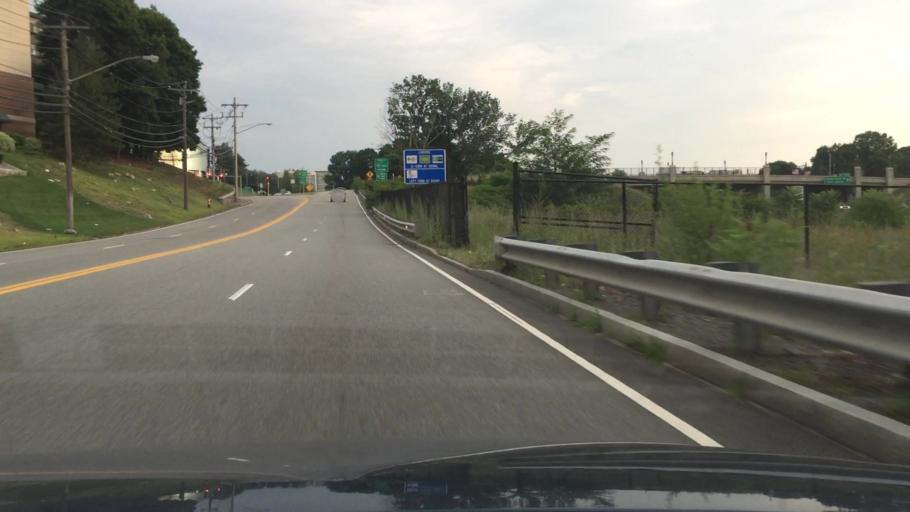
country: US
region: Massachusetts
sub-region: Middlesex County
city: Waltham
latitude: 42.3992
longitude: -71.2593
